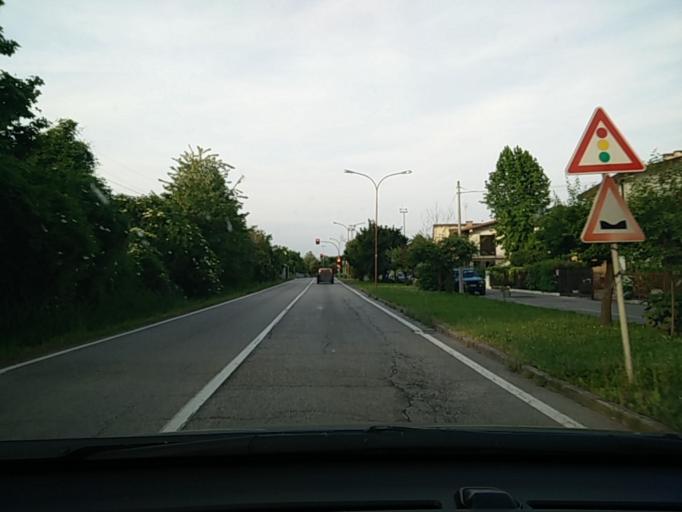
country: IT
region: Veneto
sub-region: Provincia di Venezia
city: Quarto d'Altino
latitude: 45.5785
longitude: 12.3722
